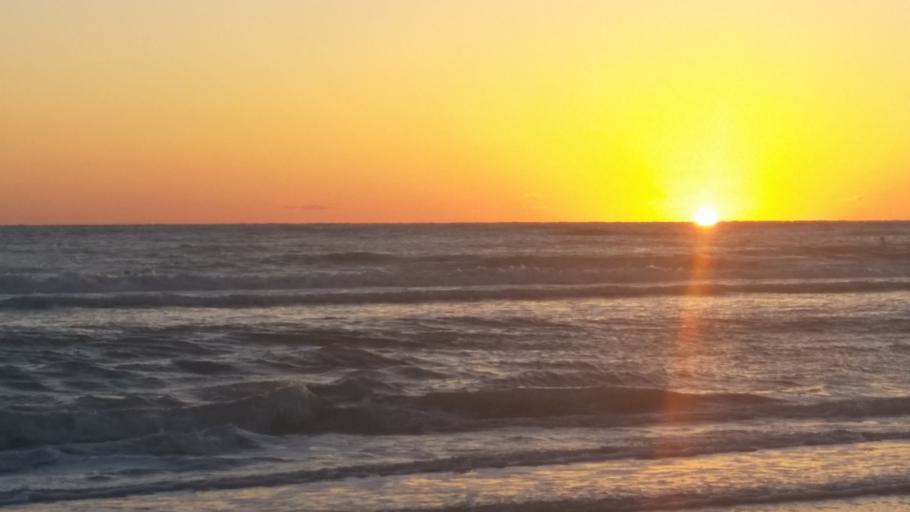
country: US
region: Florida
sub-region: Sarasota County
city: South Sarasota
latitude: 27.2654
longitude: -82.5553
